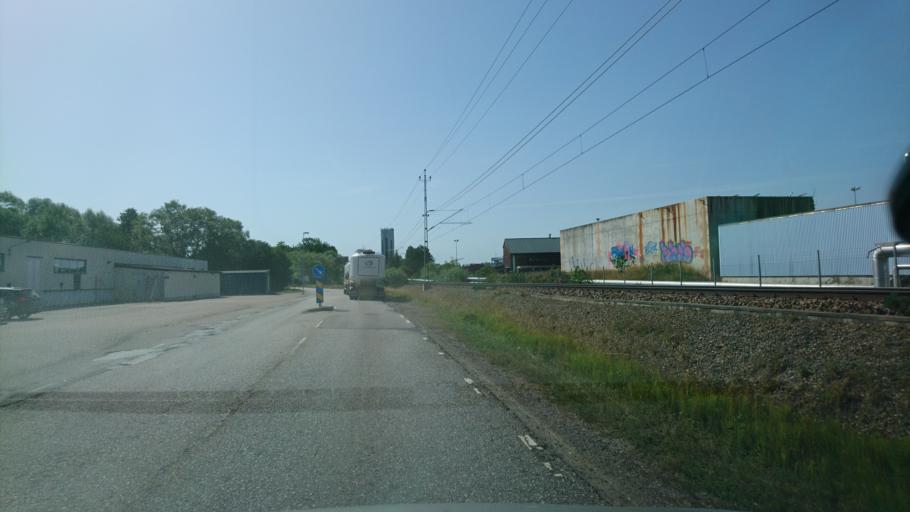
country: SE
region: Soedermanland
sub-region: Strangnas Kommun
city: Strangnas
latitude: 59.3576
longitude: 17.0392
